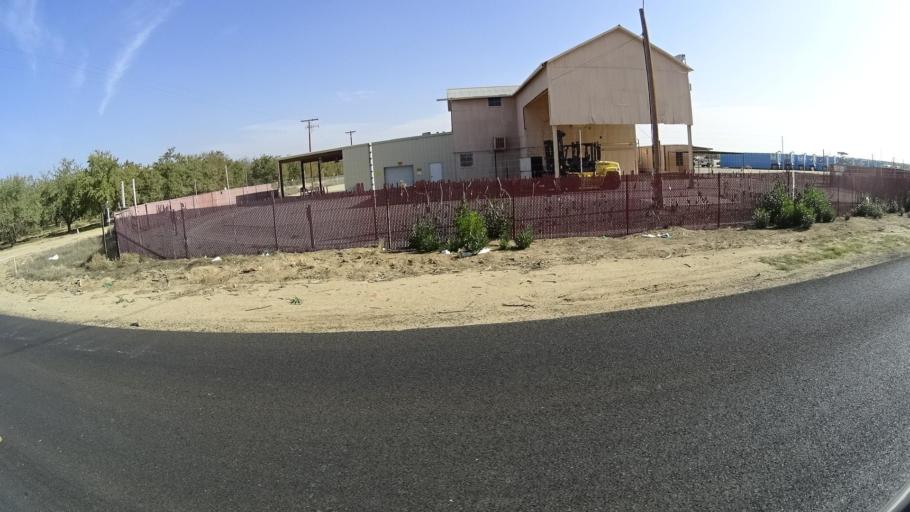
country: US
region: California
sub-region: Kern County
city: Shafter
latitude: 35.5212
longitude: -119.1518
